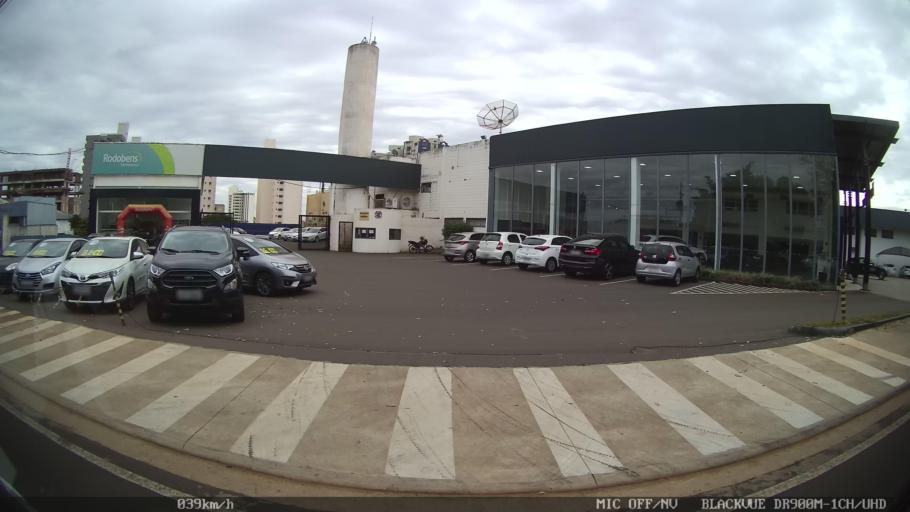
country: BR
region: Sao Paulo
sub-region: Sao Jose Do Rio Preto
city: Sao Jose do Rio Preto
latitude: -20.8230
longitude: -49.3953
